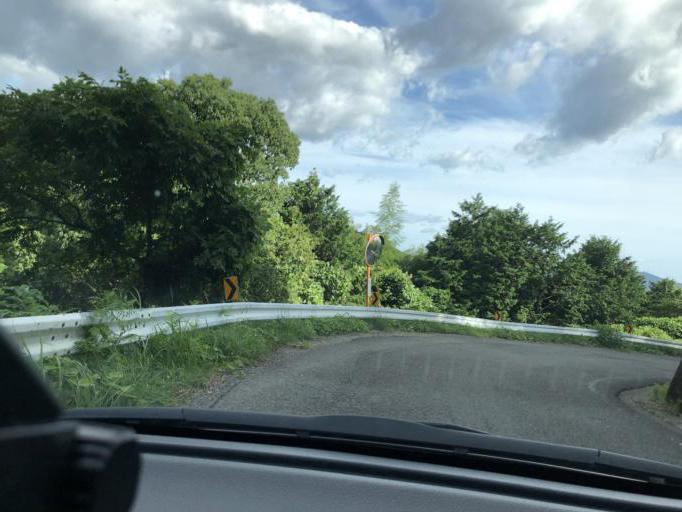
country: JP
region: Kochi
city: Kochi-shi
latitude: 33.5972
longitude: 133.5093
